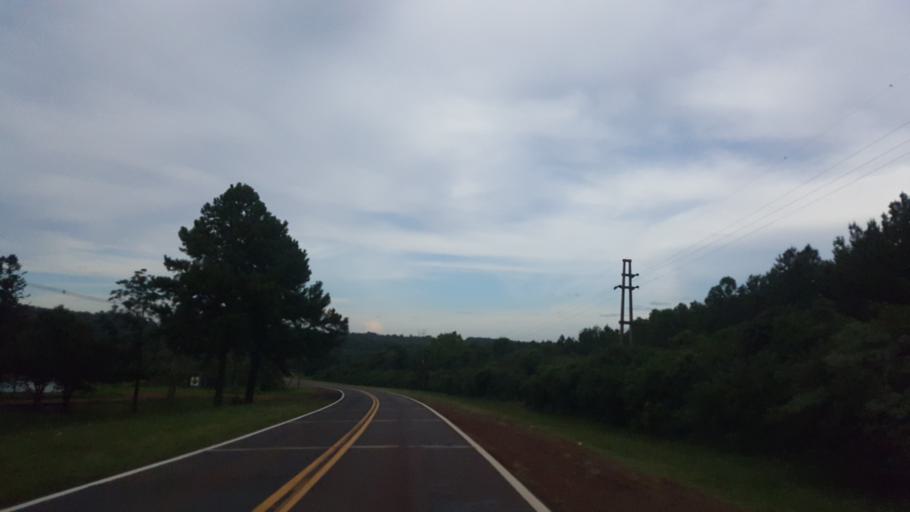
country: AR
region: Misiones
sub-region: Departamento de San Ignacio
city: San Ignacio
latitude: -27.2554
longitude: -55.5254
